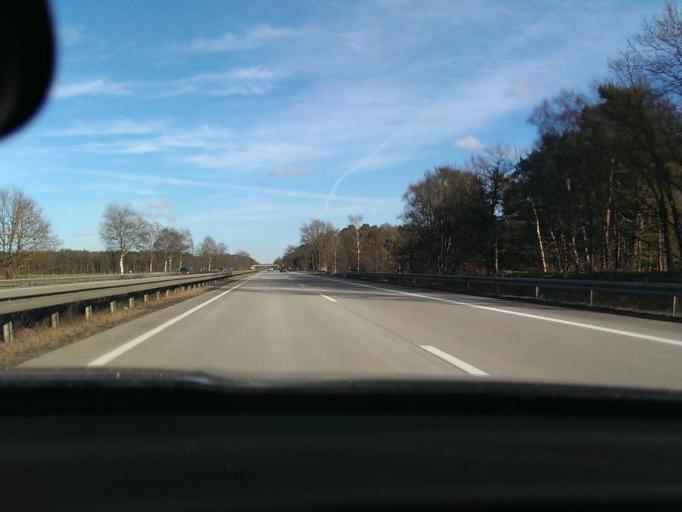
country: DE
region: Lower Saxony
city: Elze
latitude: 52.5232
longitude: 9.7814
